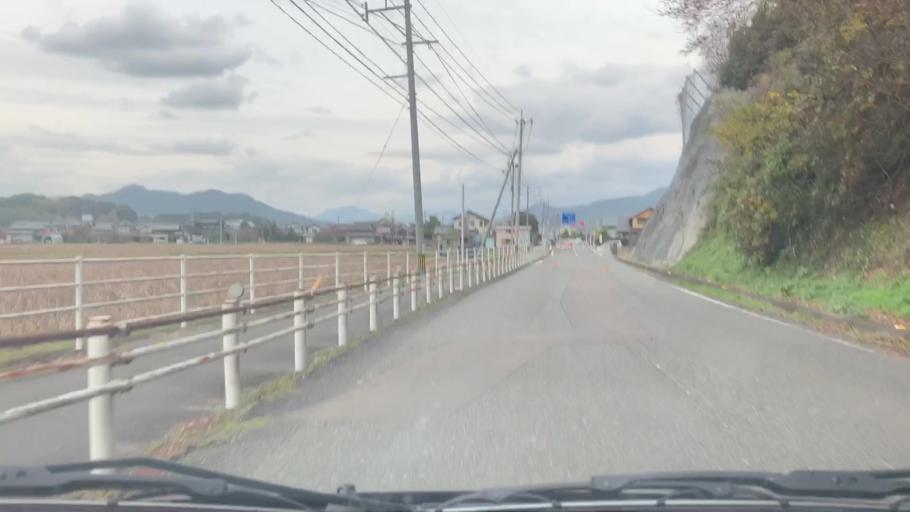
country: JP
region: Saga Prefecture
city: Kashima
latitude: 33.1196
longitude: 130.0635
